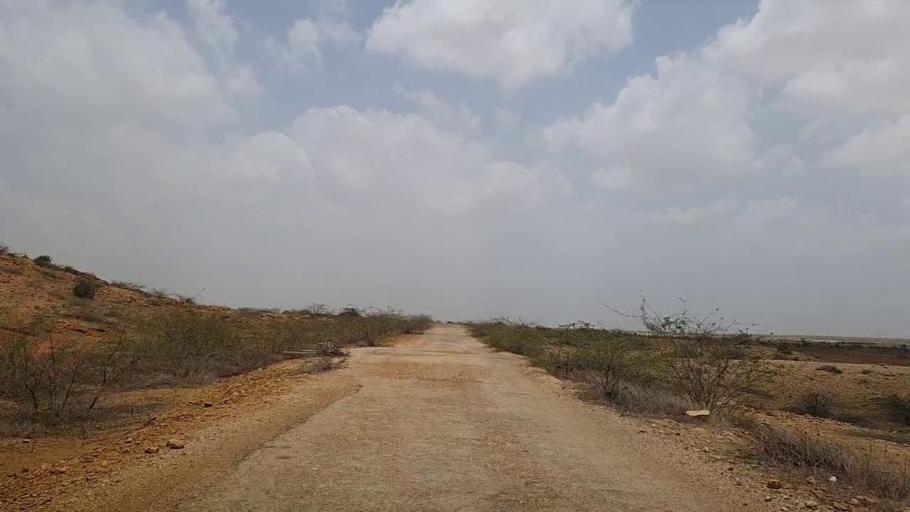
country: PK
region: Sindh
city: Thatta
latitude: 24.8960
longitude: 67.8977
